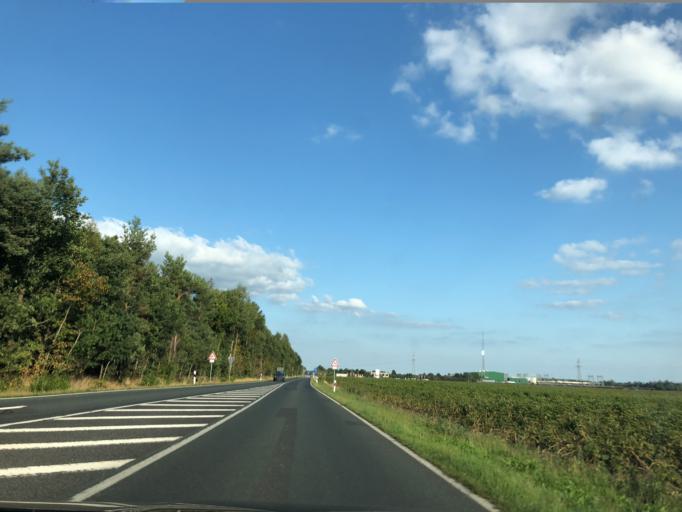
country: DE
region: Lower Saxony
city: Dersum
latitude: 52.9878
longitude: 7.2377
